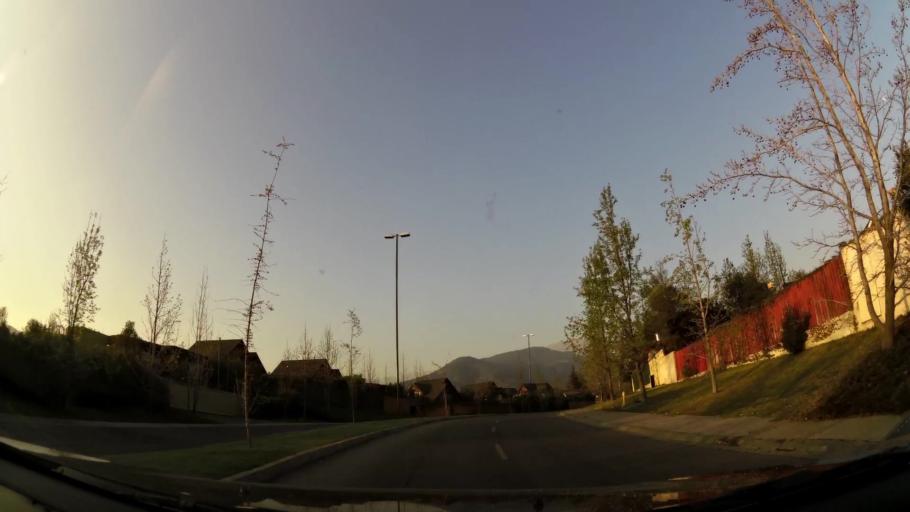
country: CL
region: Santiago Metropolitan
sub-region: Provincia de Chacabuco
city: Chicureo Abajo
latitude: -33.3301
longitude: -70.5408
